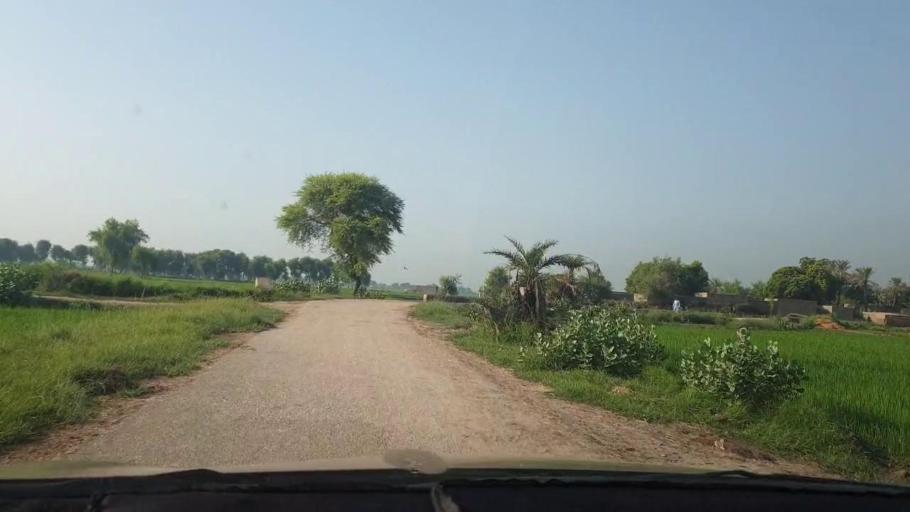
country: PK
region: Sindh
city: Kambar
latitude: 27.5726
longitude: 68.1024
